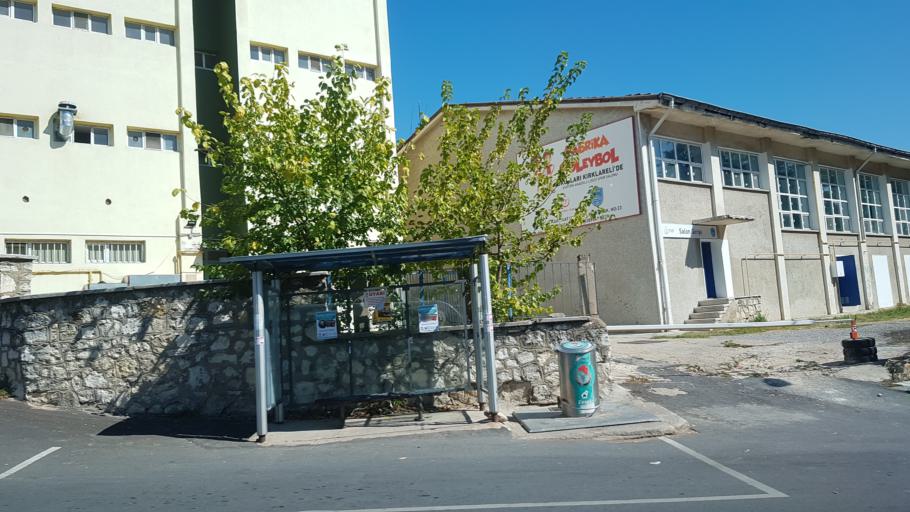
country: TR
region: Kirklareli
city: Kirklareli
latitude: 41.7379
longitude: 27.2180
